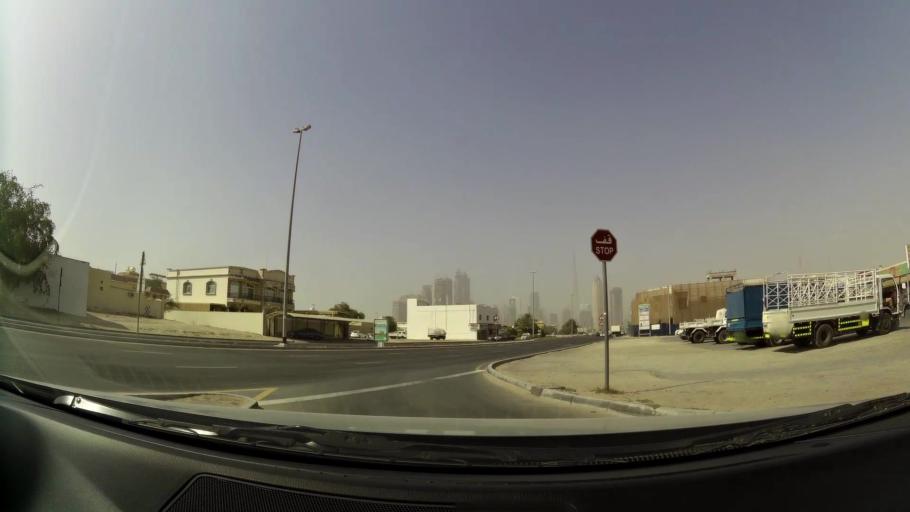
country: AE
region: Dubai
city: Dubai
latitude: 25.1677
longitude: 55.2500
